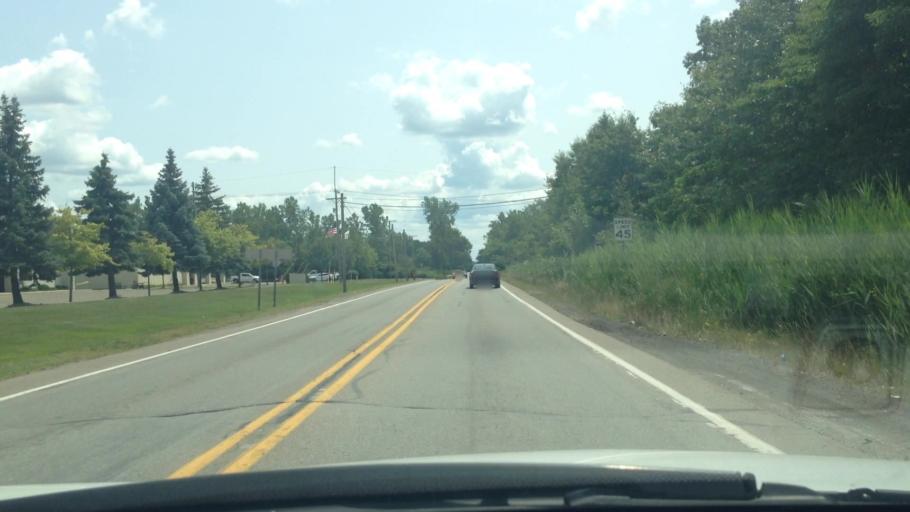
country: US
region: Michigan
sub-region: Wayne County
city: Taylor
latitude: 42.2093
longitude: -83.3070
